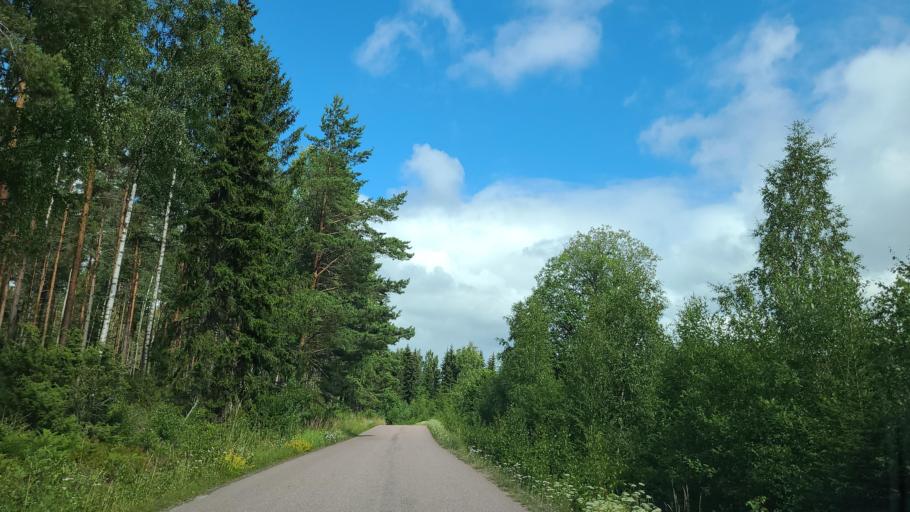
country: FI
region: Varsinais-Suomi
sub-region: Aboland-Turunmaa
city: Nagu
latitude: 60.1785
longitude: 22.0488
